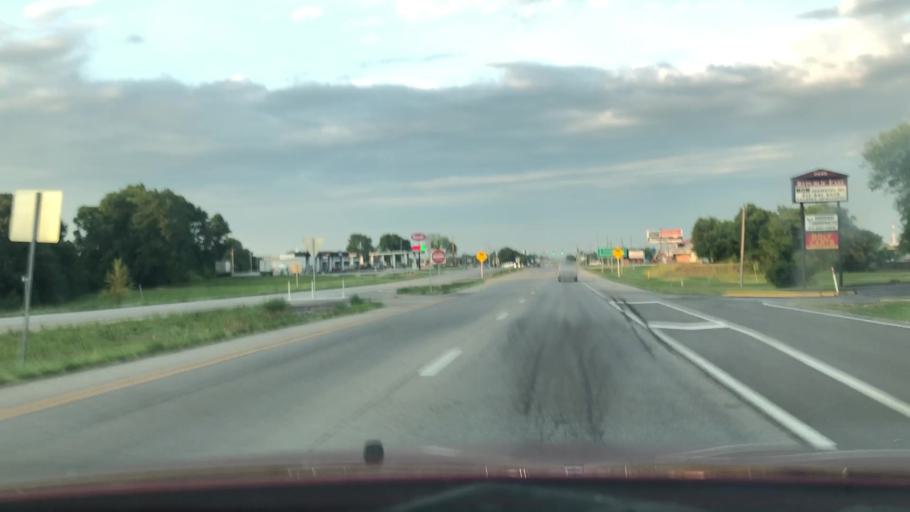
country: US
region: Missouri
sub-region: Greene County
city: Republic
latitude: 37.1439
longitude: -93.4324
